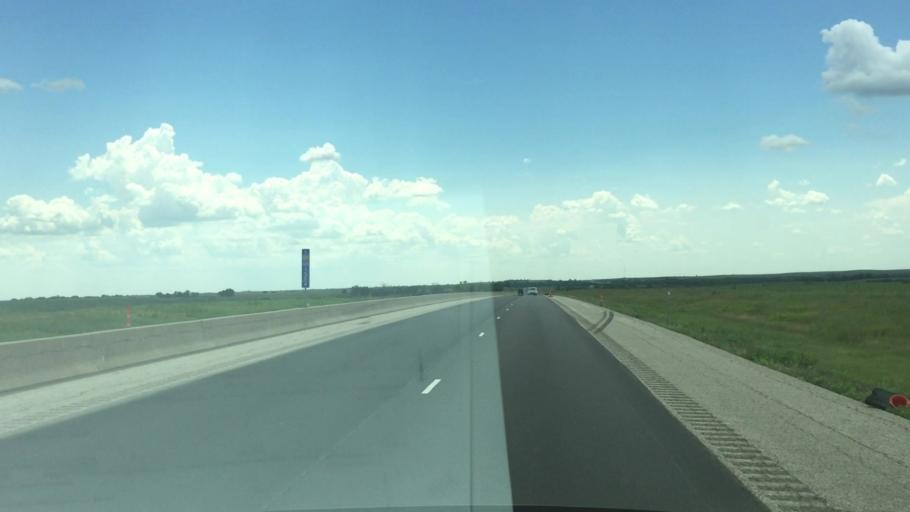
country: US
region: Kansas
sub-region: Osage County
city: Osage City
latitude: 38.6927
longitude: -95.9939
